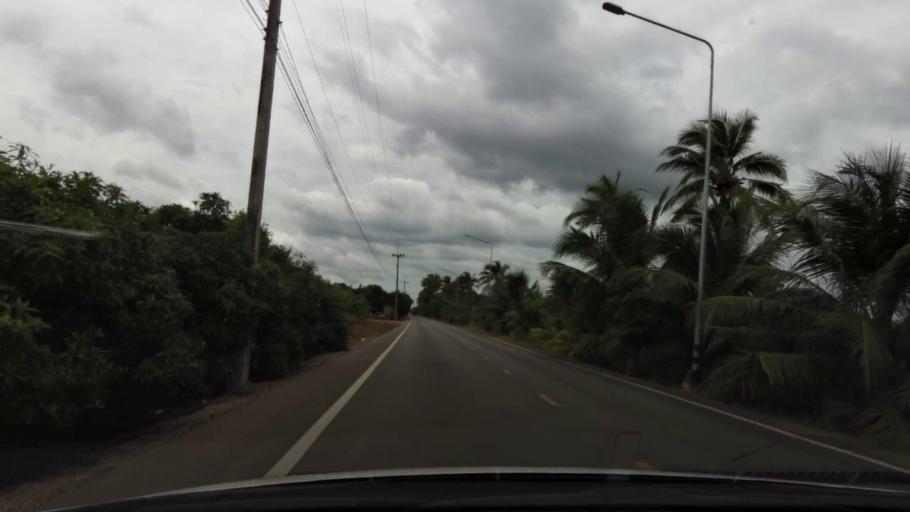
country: TH
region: Ratchaburi
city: Damnoen Saduak
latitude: 13.5569
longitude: 100.0150
